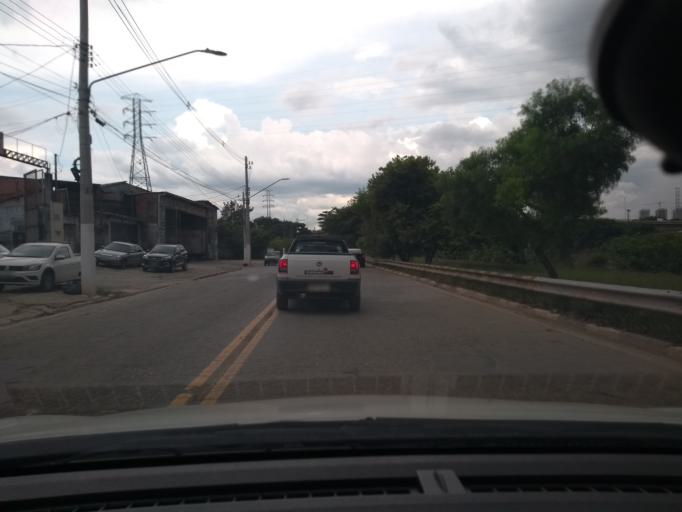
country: BR
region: Sao Paulo
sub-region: Osasco
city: Osasco
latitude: -23.5215
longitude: -46.7919
